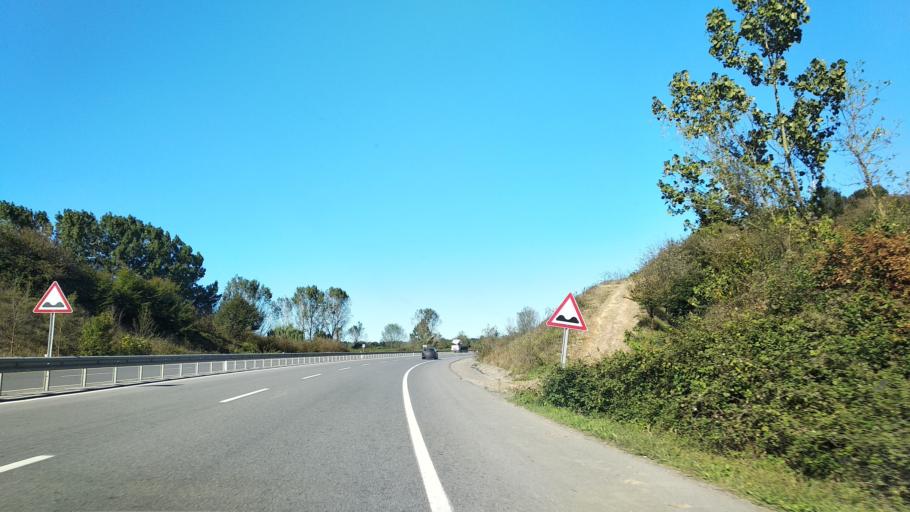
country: TR
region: Sakarya
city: Karasu
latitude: 41.0601
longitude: 30.6372
